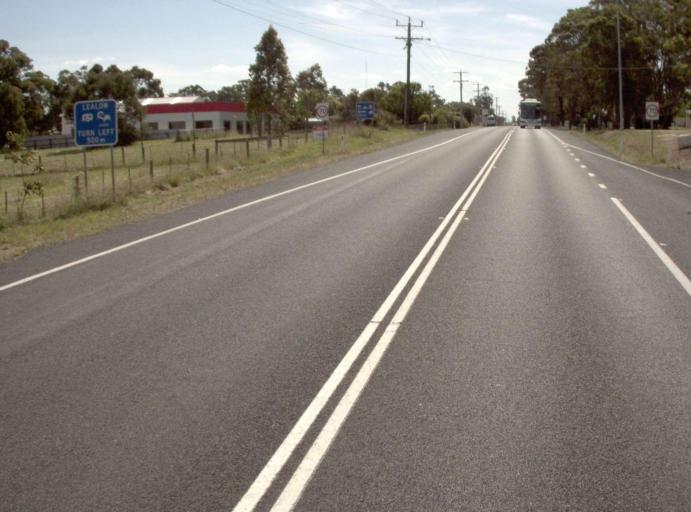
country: AU
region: Victoria
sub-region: East Gippsland
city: Lakes Entrance
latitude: -37.8206
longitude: 147.8348
